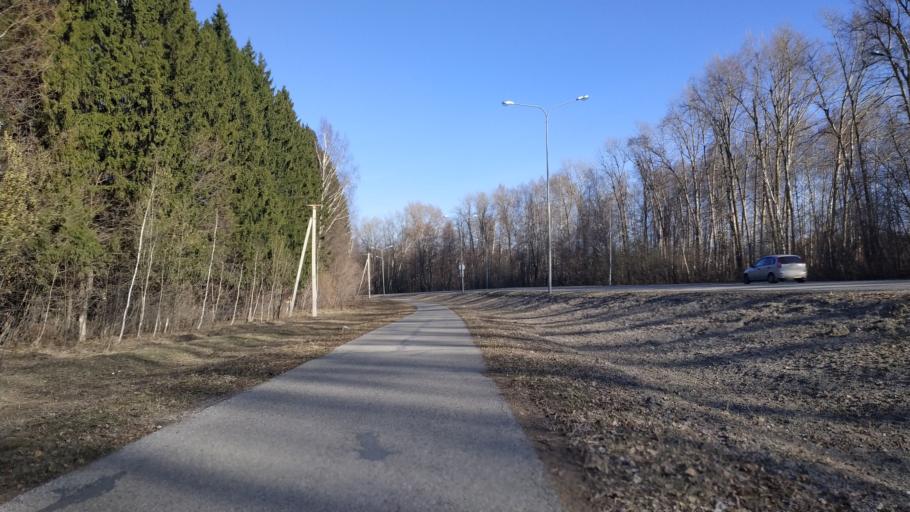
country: RU
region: Chuvashia
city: Novyye Lapsary
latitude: 56.1286
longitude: 47.1194
